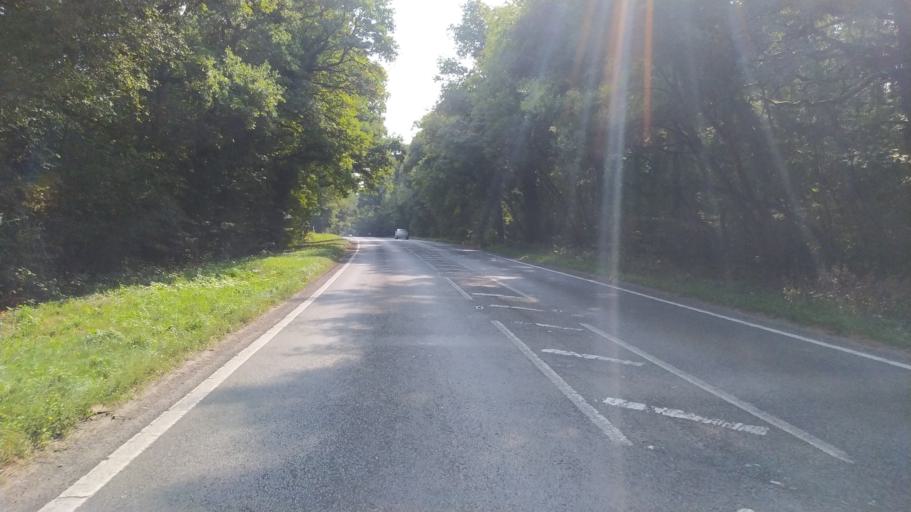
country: GB
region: England
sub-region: Hampshire
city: Odiham
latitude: 51.2495
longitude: -0.8974
